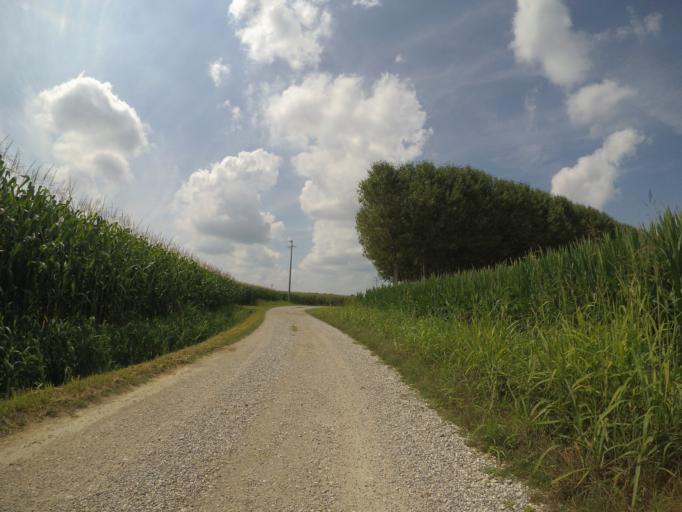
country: IT
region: Friuli Venezia Giulia
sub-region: Provincia di Udine
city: Rivignano
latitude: 45.8928
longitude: 13.0185
